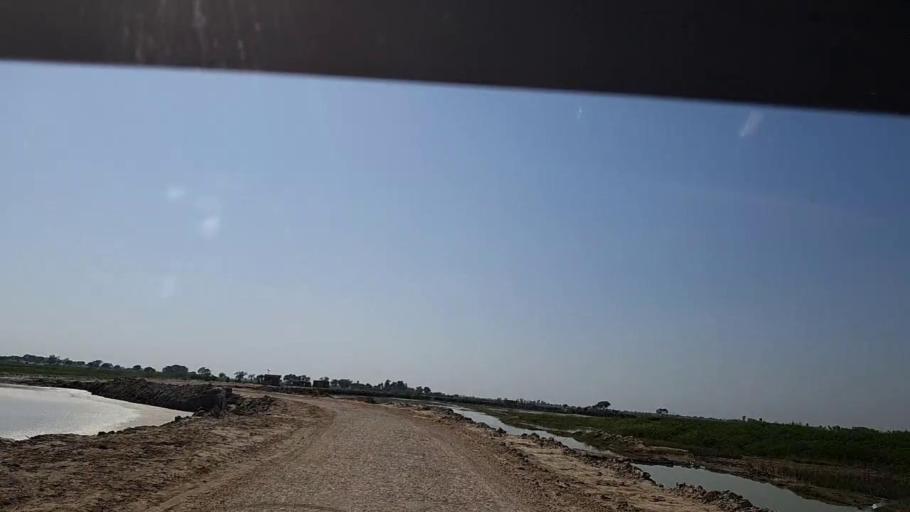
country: PK
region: Sindh
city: Tangwani
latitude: 28.3172
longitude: 69.0857
